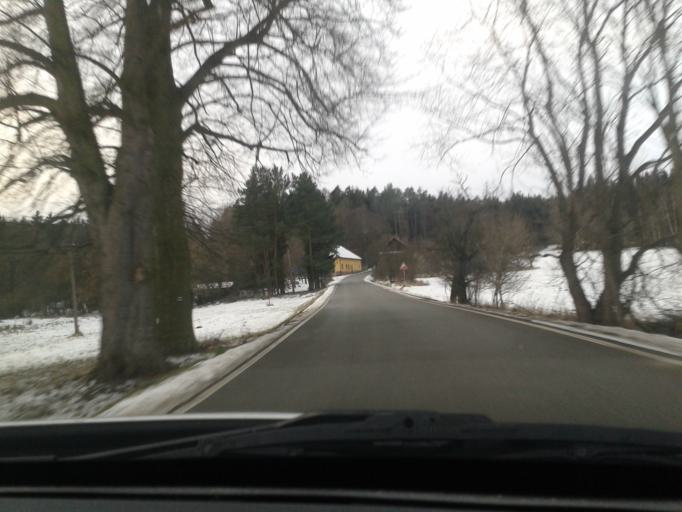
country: CZ
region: Olomoucky
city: Pteni
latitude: 49.5101
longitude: 16.9250
